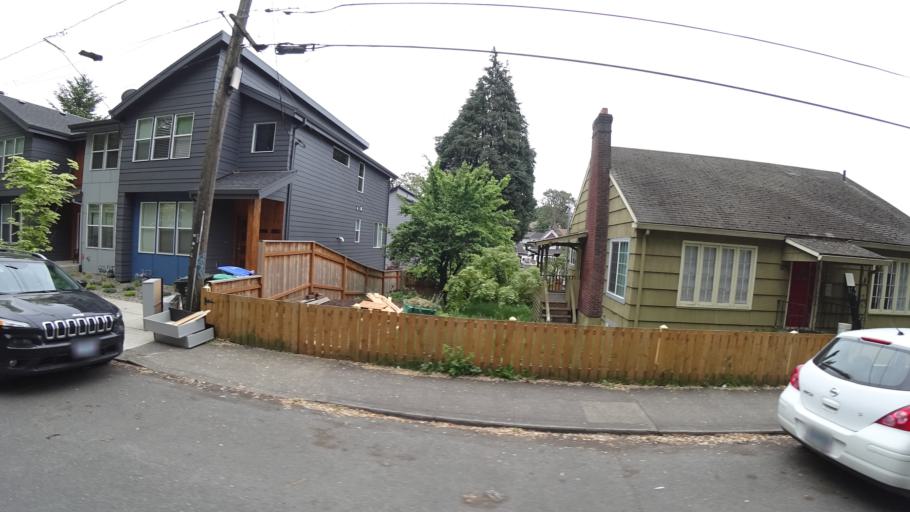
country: US
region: Oregon
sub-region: Multnomah County
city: Portland
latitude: 45.5170
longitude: -122.6411
